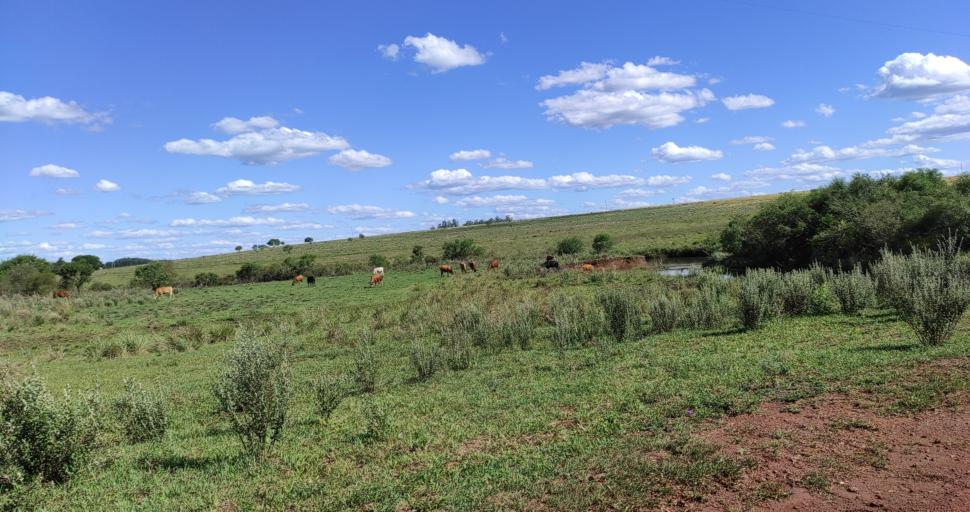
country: PY
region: Itapua
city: San Juan del Parana
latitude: -27.4453
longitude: -56.0629
